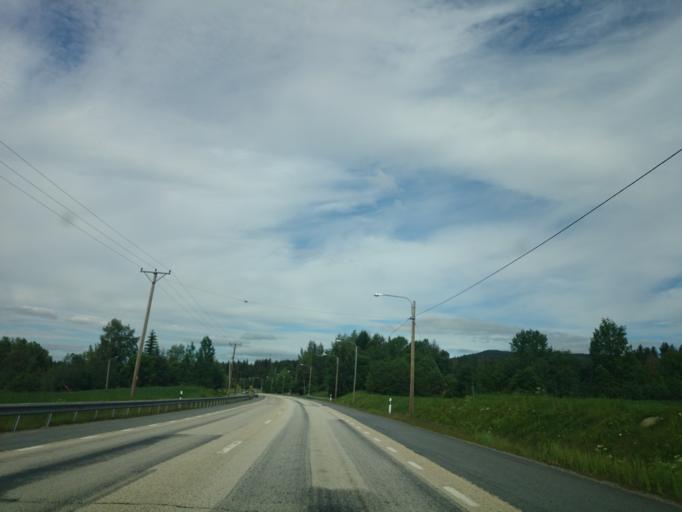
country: SE
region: Vaesternorrland
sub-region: Sundsvalls Kommun
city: Matfors
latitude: 62.4092
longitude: 16.6736
